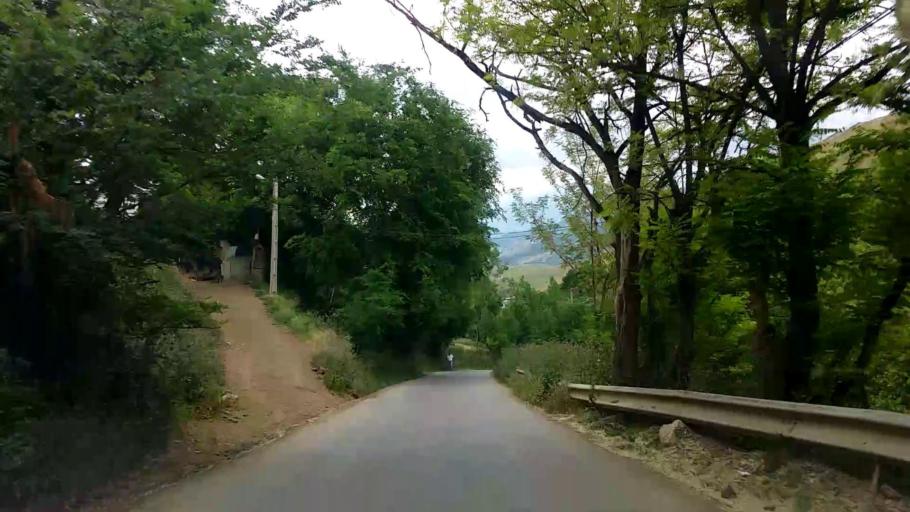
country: IR
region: Mazandaran
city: Chalus
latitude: 36.5201
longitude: 51.2602
